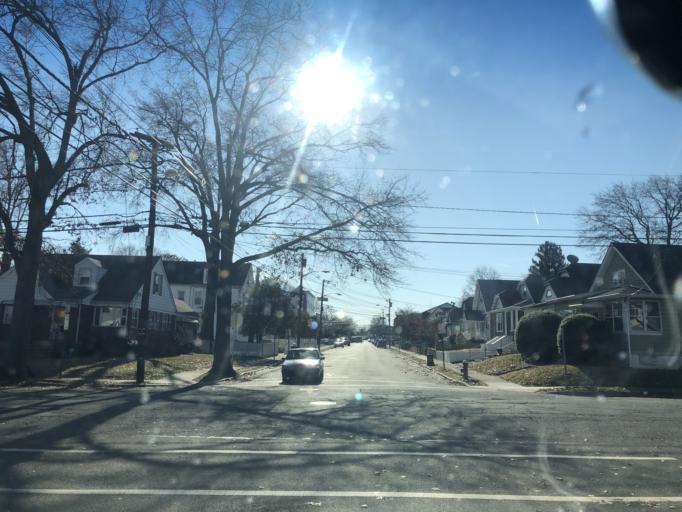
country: US
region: New Jersey
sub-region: Bergen County
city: Fair Lawn
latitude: 40.9263
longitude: -74.1446
